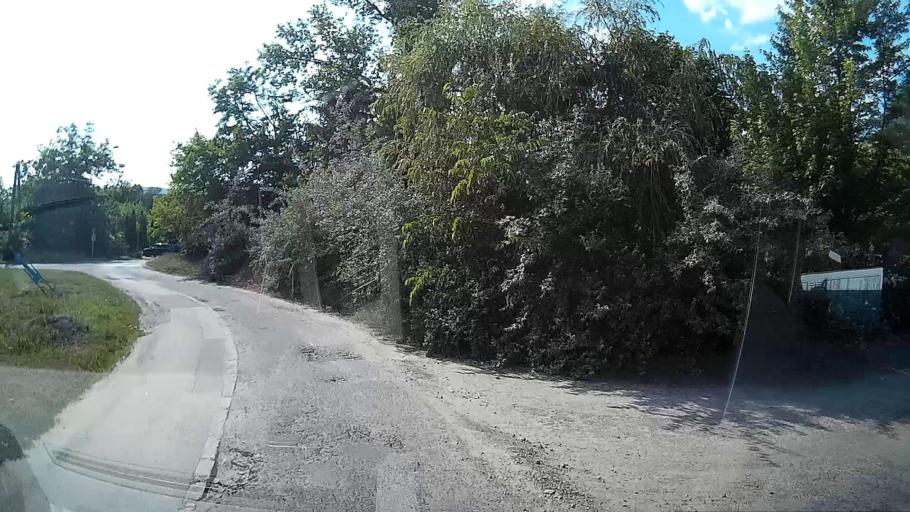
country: HU
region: Pest
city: Leanyfalu
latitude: 47.7138
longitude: 19.1141
